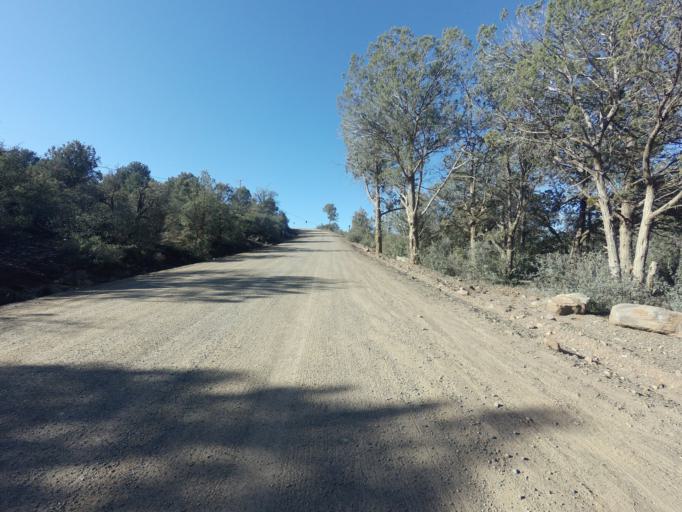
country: US
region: Arizona
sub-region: Gila County
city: Payson
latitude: 34.3026
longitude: -111.3521
